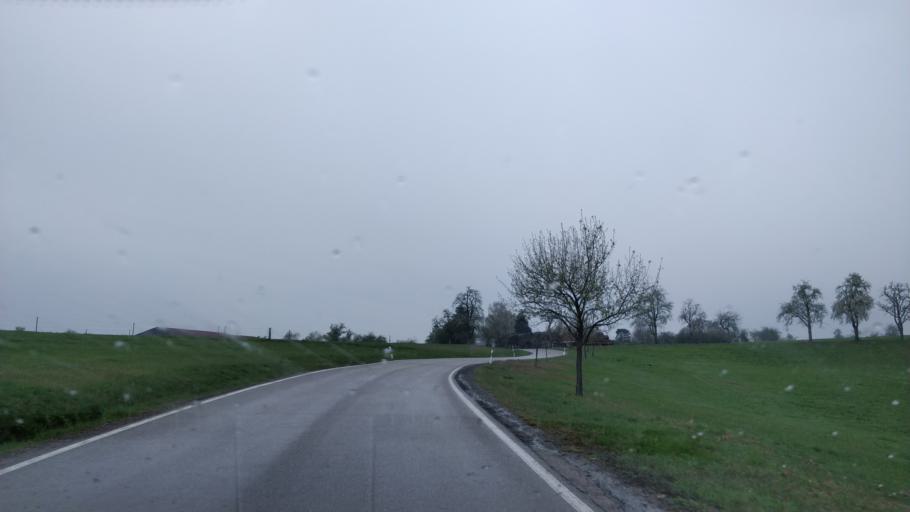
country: DE
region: Baden-Wuerttemberg
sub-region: Regierungsbezirk Stuttgart
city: Mainhardt
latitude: 49.0443
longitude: 9.5940
